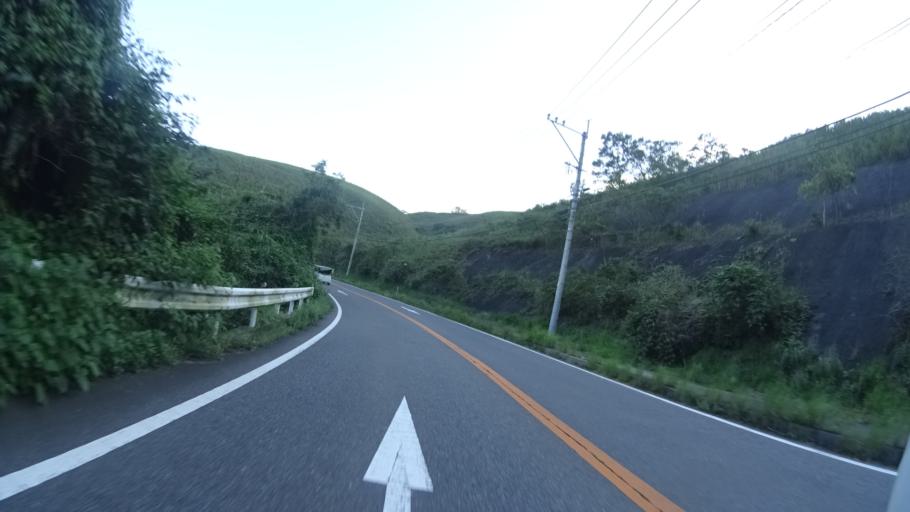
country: JP
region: Oita
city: Beppu
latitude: 33.3429
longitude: 131.4558
